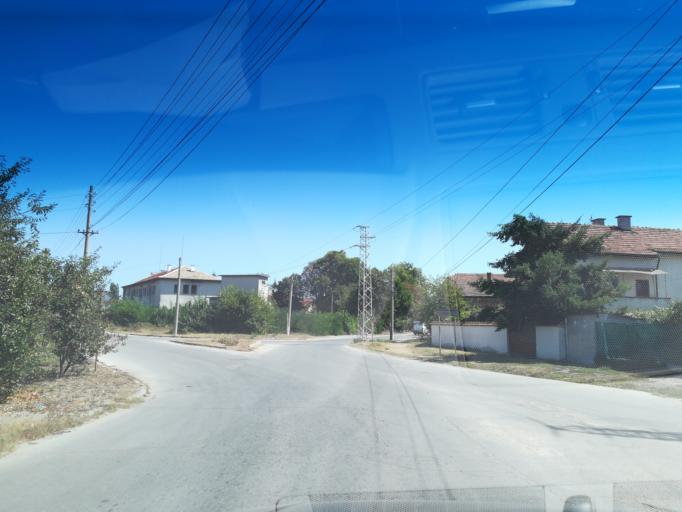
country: BG
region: Pazardzhik
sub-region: Obshtina Pazardzhik
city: Pazardzhik
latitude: 42.2510
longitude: 24.4255
